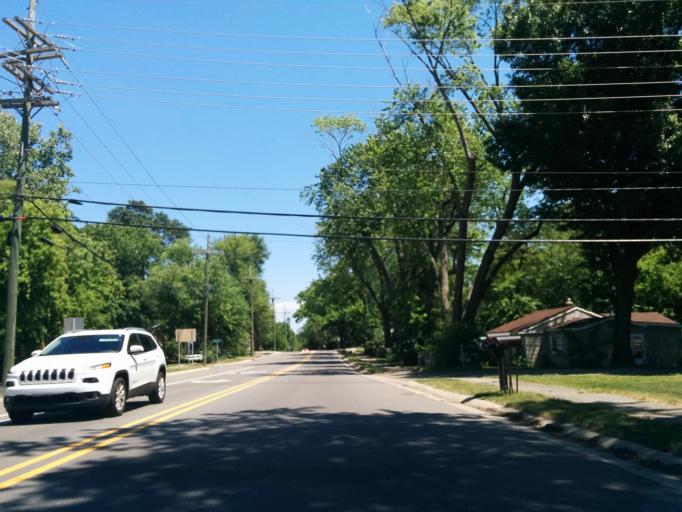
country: US
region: Michigan
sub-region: Oakland County
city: West Bloomfield Township
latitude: 42.5746
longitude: -83.4210
